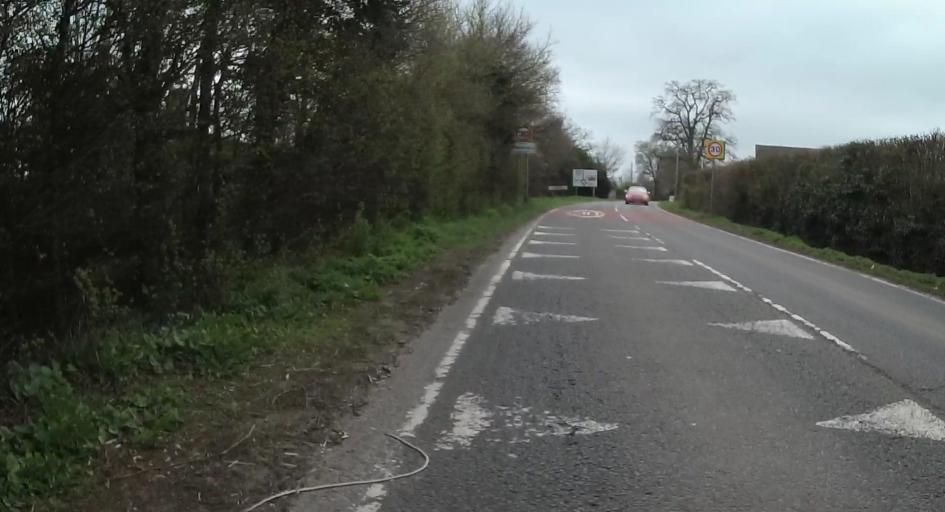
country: GB
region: England
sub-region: West Berkshire
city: Arborfield
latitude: 51.4000
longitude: -0.9063
